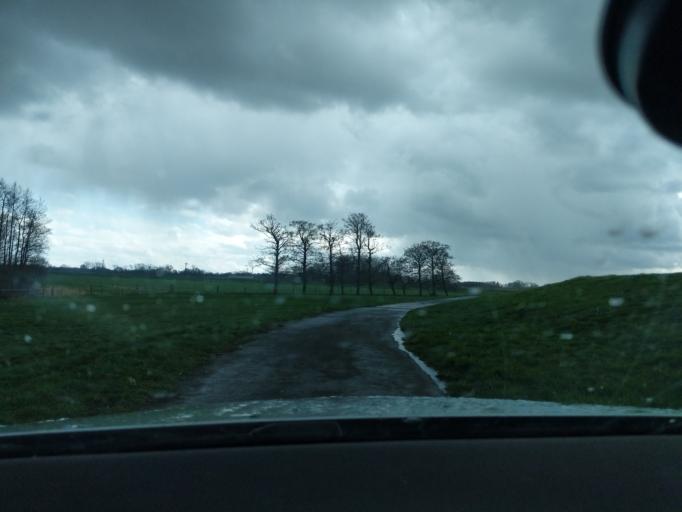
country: DE
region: Lower Saxony
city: Kranenburg
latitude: 53.6225
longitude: 9.2048
